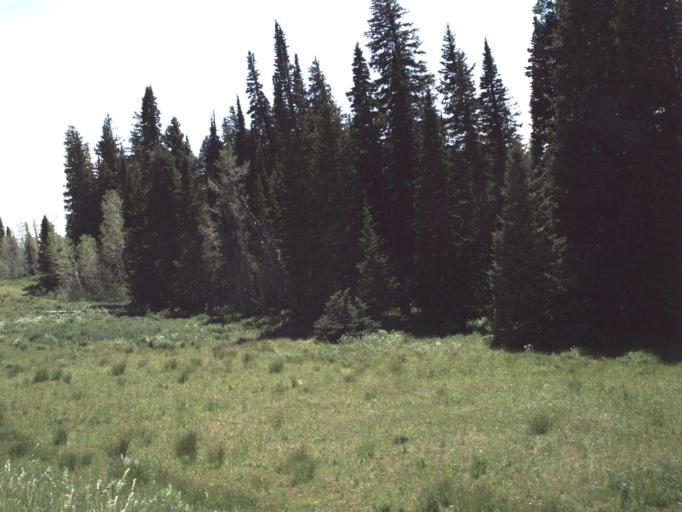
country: US
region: Utah
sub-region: Weber County
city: Wolf Creek
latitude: 41.4406
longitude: -111.5041
